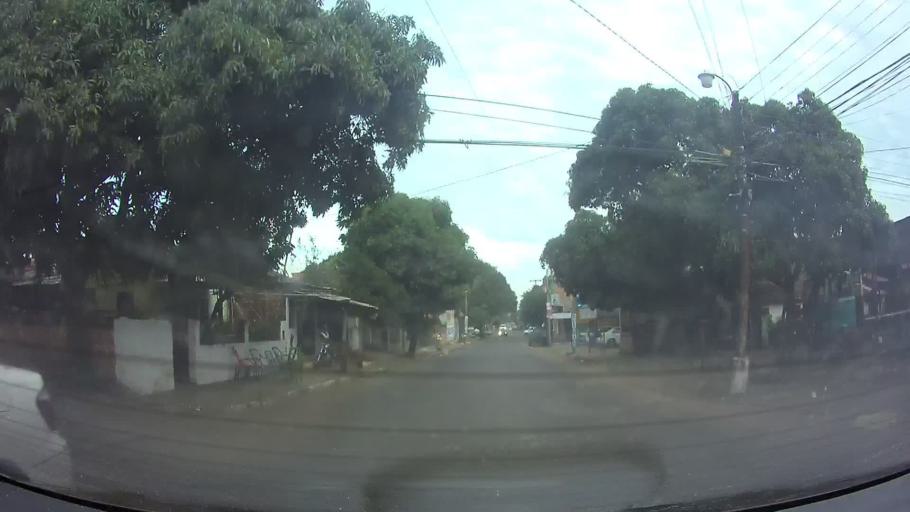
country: PY
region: Central
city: Villa Elisa
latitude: -25.3392
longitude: -57.5716
